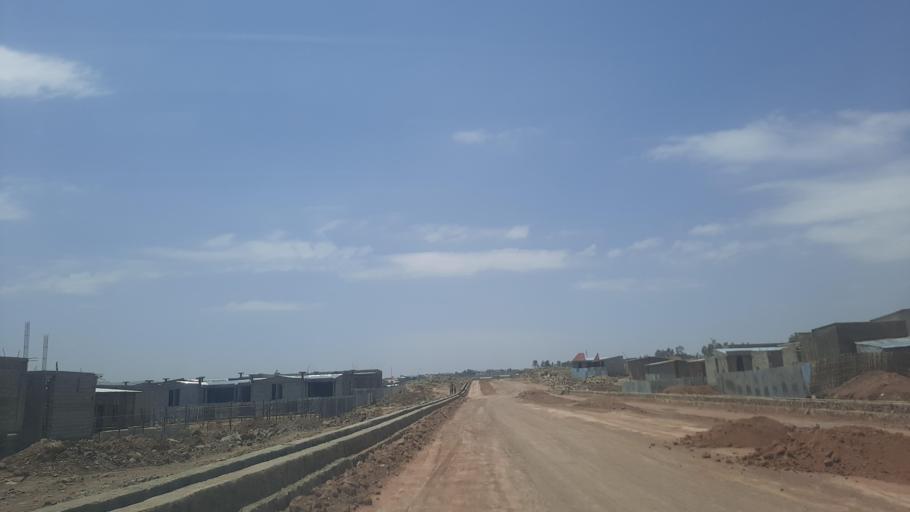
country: ET
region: Southern Nations, Nationalities, and People's Region
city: Butajira
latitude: 7.8488
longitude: 38.1782
